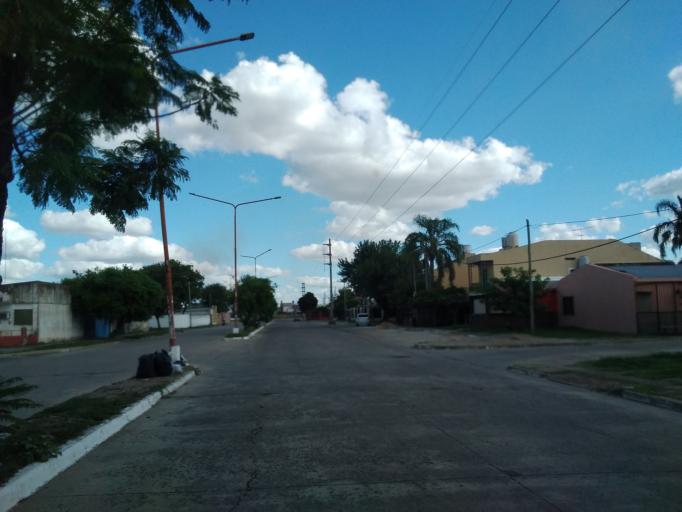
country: AR
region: Corrientes
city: Corrientes
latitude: -27.4975
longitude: -58.8272
